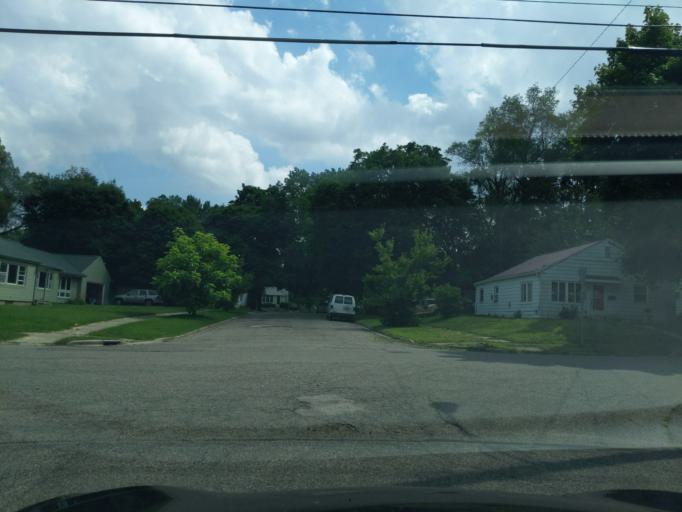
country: US
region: Michigan
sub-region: Ingham County
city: Lansing
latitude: 42.7166
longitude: -84.5698
